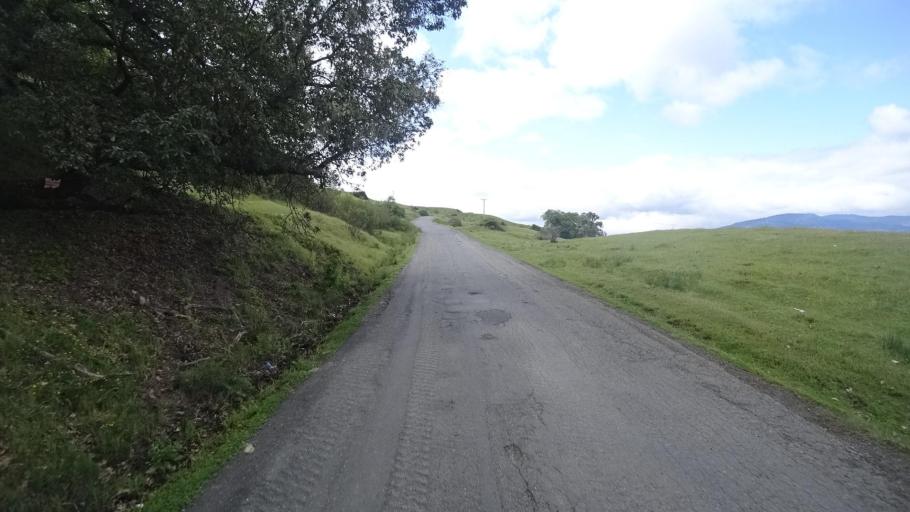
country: US
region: California
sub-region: Humboldt County
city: Redway
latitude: 40.1810
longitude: -123.5716
